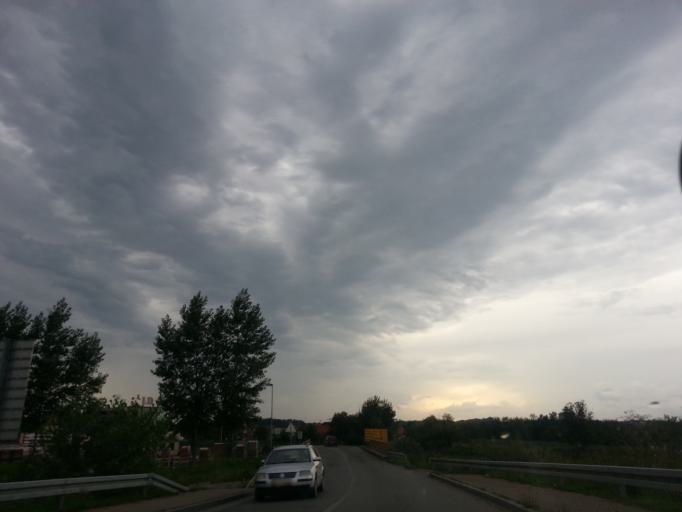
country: BA
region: Republika Srpska
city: Velika Obarska
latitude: 44.7673
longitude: 19.1725
